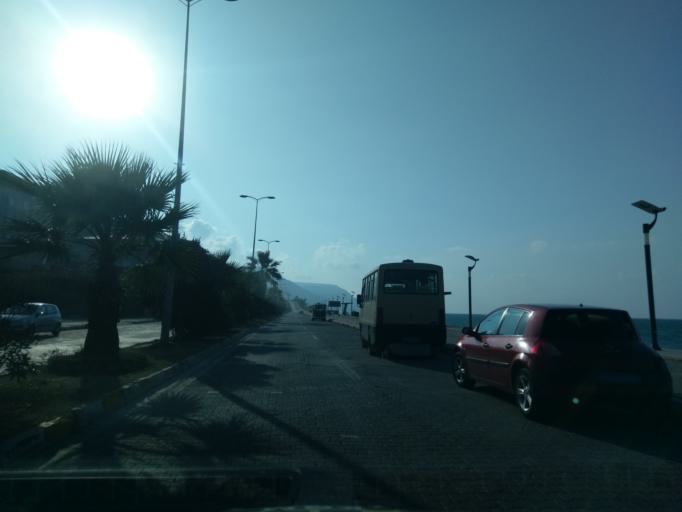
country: TR
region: Kastamonu
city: Catalzeytin
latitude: 41.9546
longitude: 34.2124
